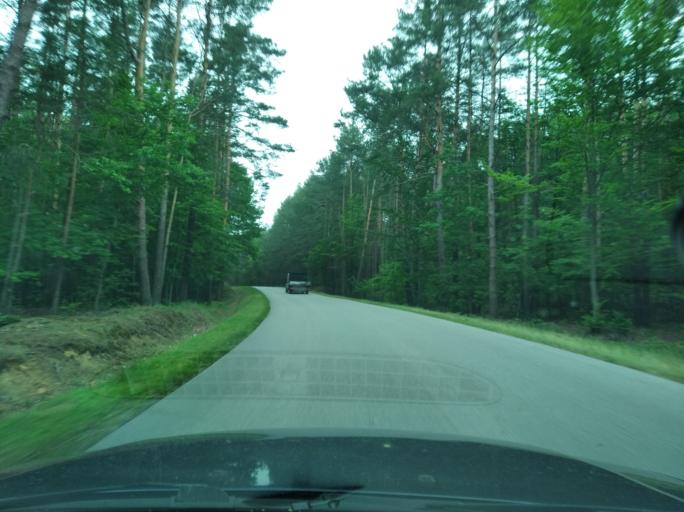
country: PL
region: Subcarpathian Voivodeship
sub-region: Powiat kolbuszowski
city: Niwiska
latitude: 50.2078
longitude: 21.6409
